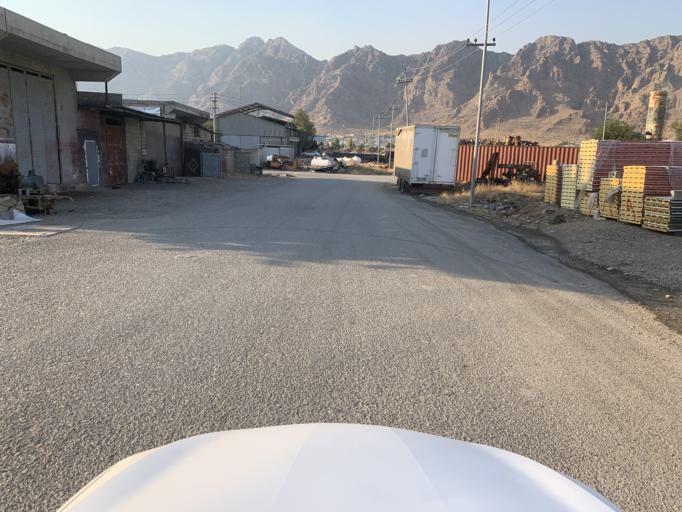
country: IQ
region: As Sulaymaniyah
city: Raniye
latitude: 36.2465
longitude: 44.8891
